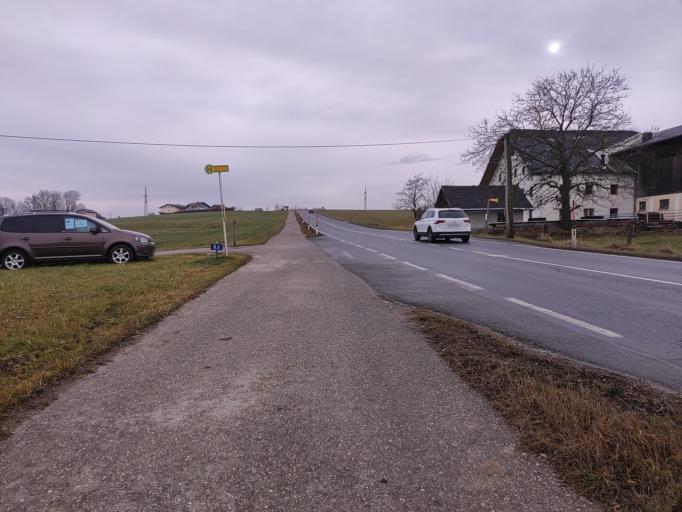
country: AT
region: Salzburg
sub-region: Politischer Bezirk Salzburg-Umgebung
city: Obertrum am See
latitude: 47.9253
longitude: 13.0937
